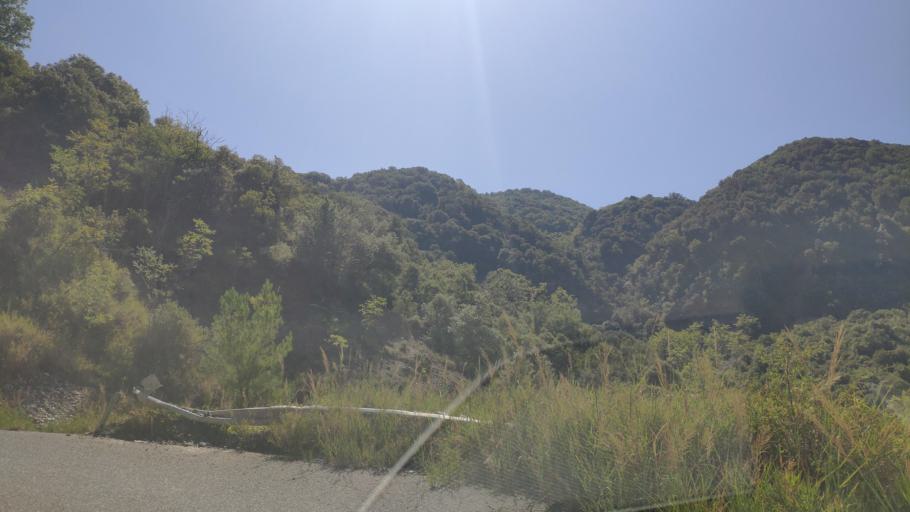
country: GR
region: Central Greece
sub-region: Nomos Evrytanias
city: Kerasochori
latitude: 39.0012
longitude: 21.5827
